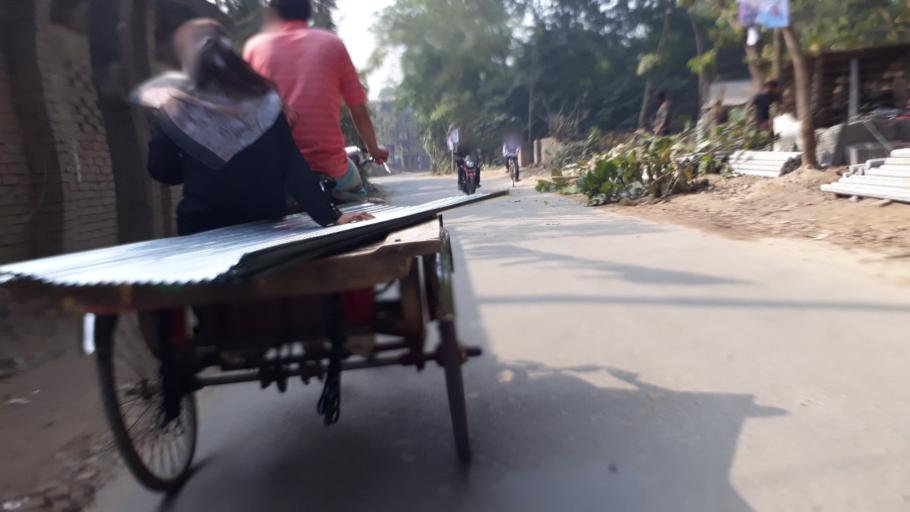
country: BD
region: Khulna
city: Kaliganj
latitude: 23.3540
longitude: 88.9088
